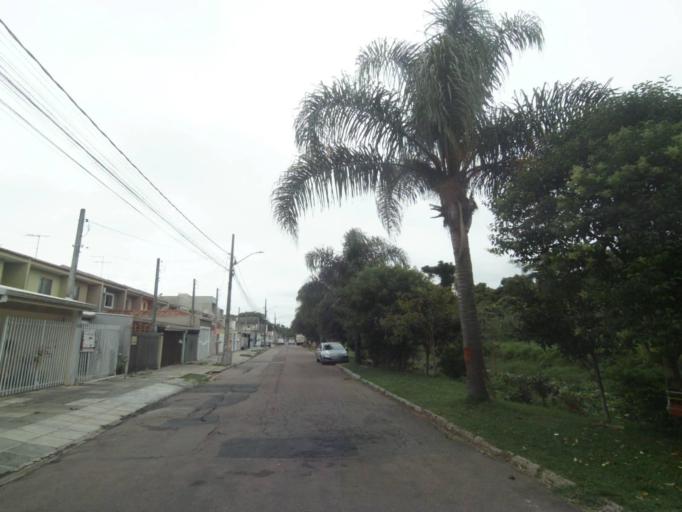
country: BR
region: Parana
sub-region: Araucaria
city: Araucaria
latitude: -25.5492
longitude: -49.3438
